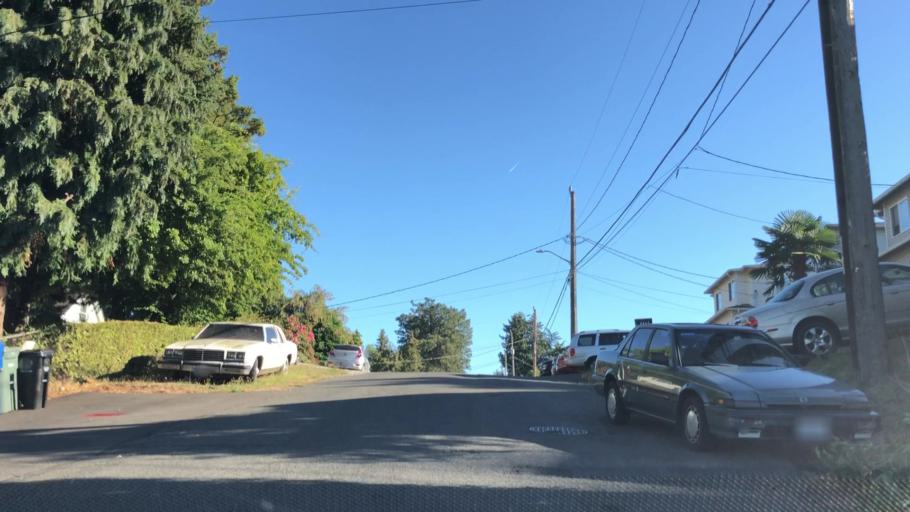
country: US
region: Washington
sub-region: King County
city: Boulevard Park
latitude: 47.5488
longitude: -122.2915
